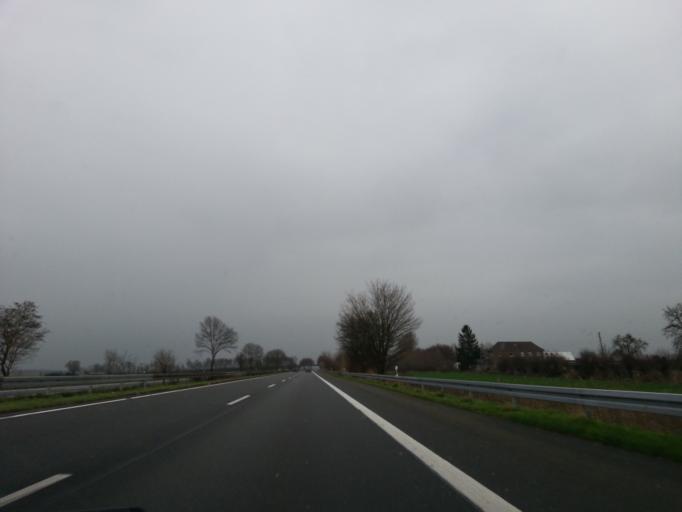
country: NL
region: Gelderland
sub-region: Oude IJsselstreek
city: Gendringen
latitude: 51.8449
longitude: 6.3223
